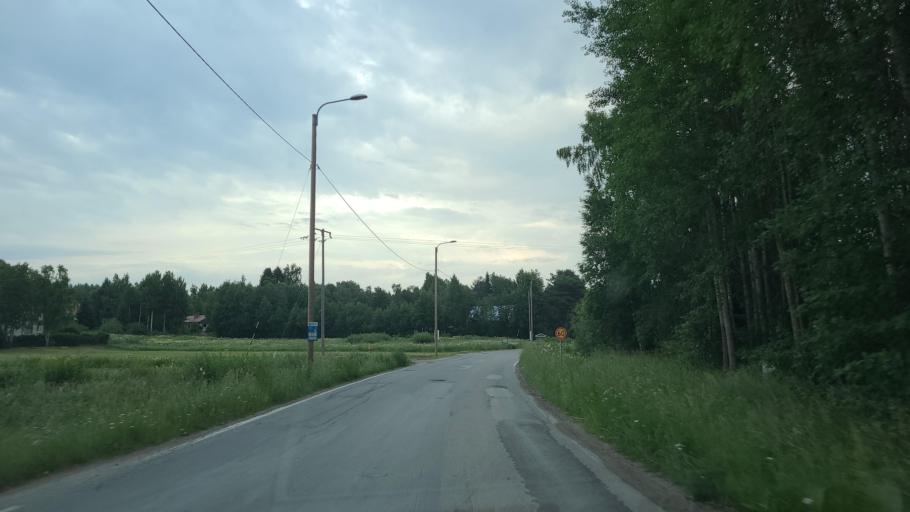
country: FI
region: Ostrobothnia
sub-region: Vaasa
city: Replot
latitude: 63.1826
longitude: 21.2825
